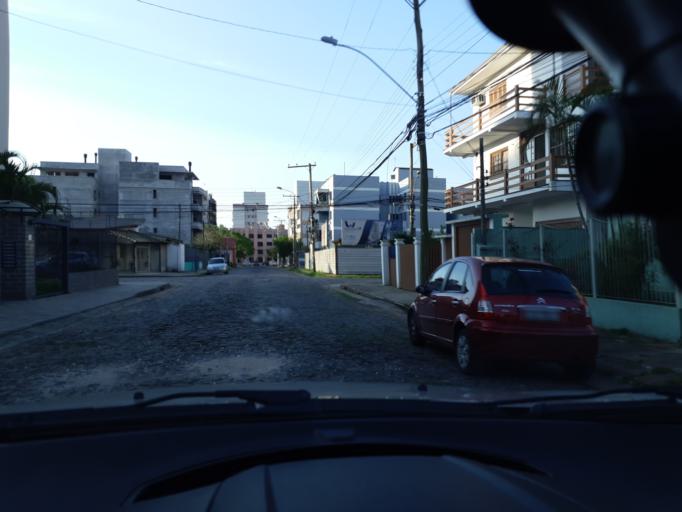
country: BR
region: Rio Grande do Sul
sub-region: Sao Leopoldo
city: Sao Leopoldo
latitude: -29.7716
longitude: -51.1402
